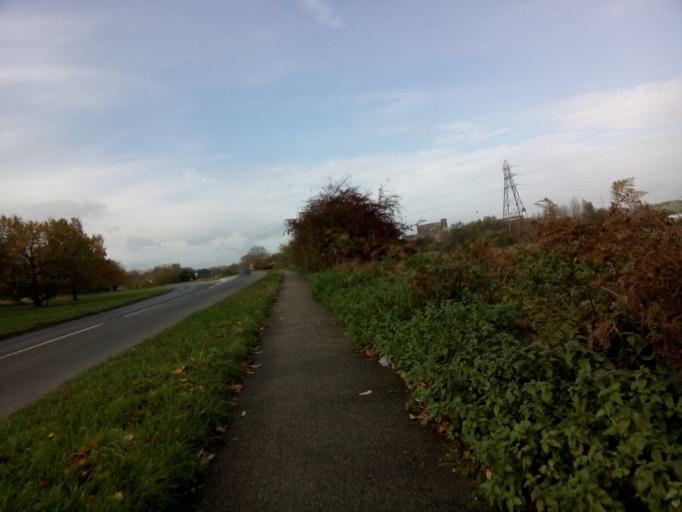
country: GB
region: England
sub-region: Suffolk
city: Needham Market
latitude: 52.1710
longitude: 1.0241
